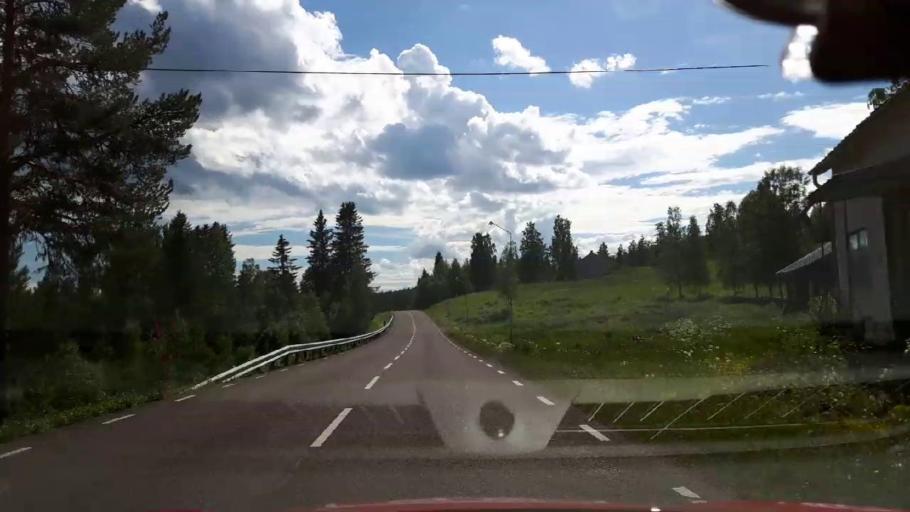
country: SE
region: Jaemtland
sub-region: Krokoms Kommun
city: Valla
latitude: 63.9873
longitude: 14.2277
